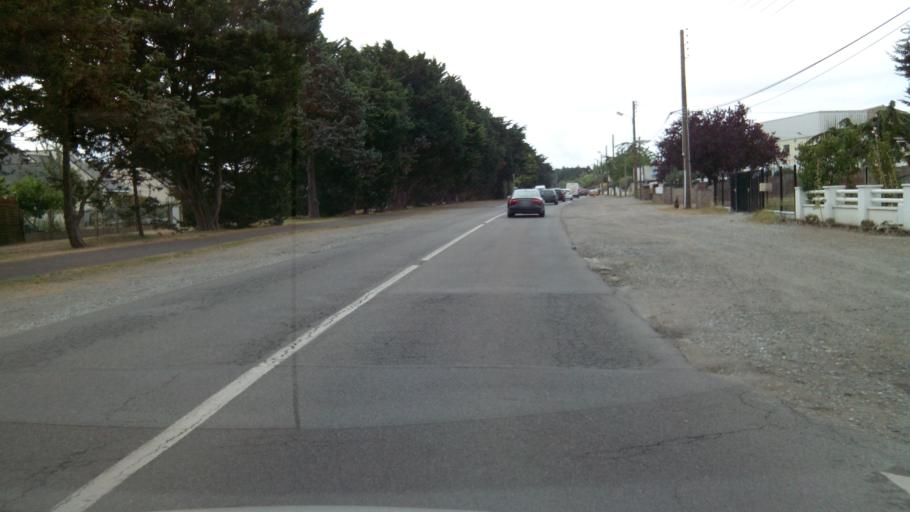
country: FR
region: Pays de la Loire
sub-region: Departement de la Loire-Atlantique
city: Le Pouliguen
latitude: 47.2768
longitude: -2.4384
